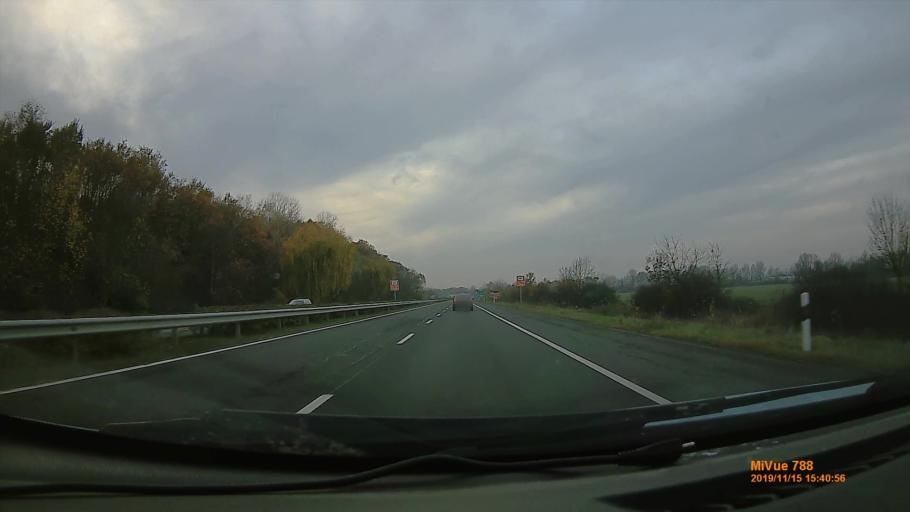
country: HU
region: Bekes
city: Bekescsaba
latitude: 46.6750
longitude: 21.1421
